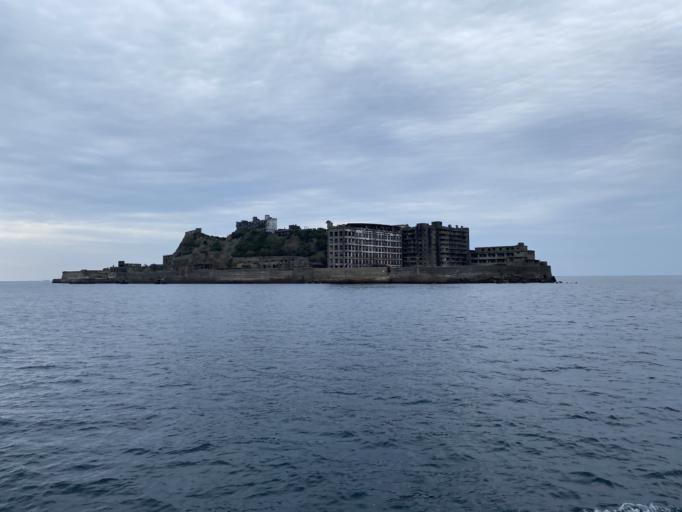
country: JP
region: Nagasaki
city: Nagasaki-shi
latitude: 32.6291
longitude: 129.7425
